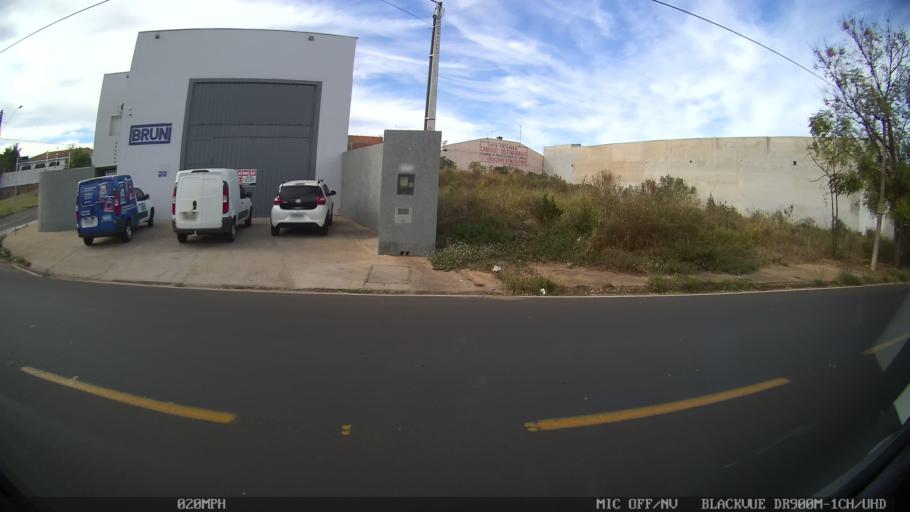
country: BR
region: Sao Paulo
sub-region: Catanduva
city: Catanduva
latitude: -21.1395
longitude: -48.9998
